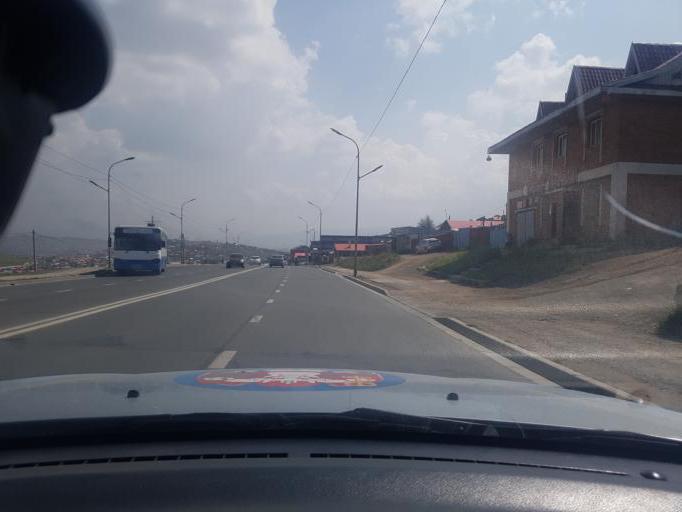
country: MN
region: Ulaanbaatar
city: Ulaanbaatar
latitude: 47.9464
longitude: 106.8682
